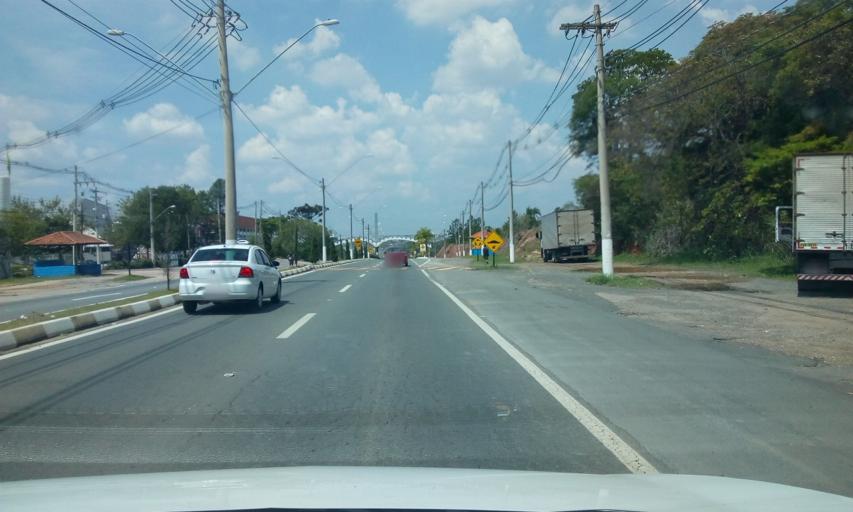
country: BR
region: Sao Paulo
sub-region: Itupeva
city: Itupeva
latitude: -23.1595
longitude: -47.0327
